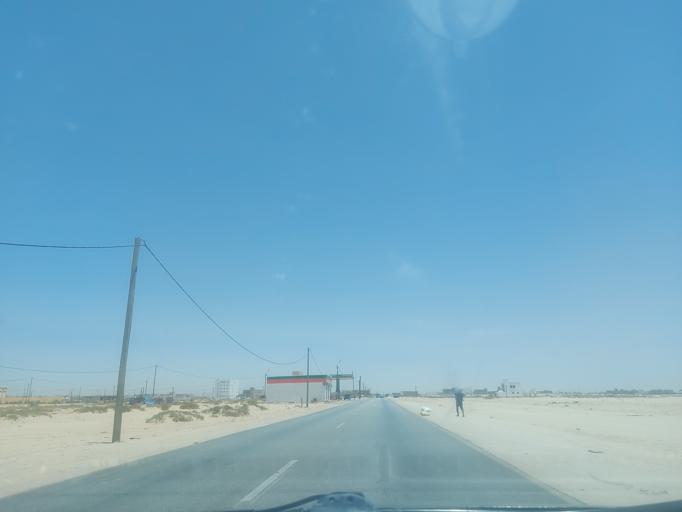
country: MR
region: Nouakchott
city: Nouakchott
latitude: 18.0809
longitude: -15.9539
